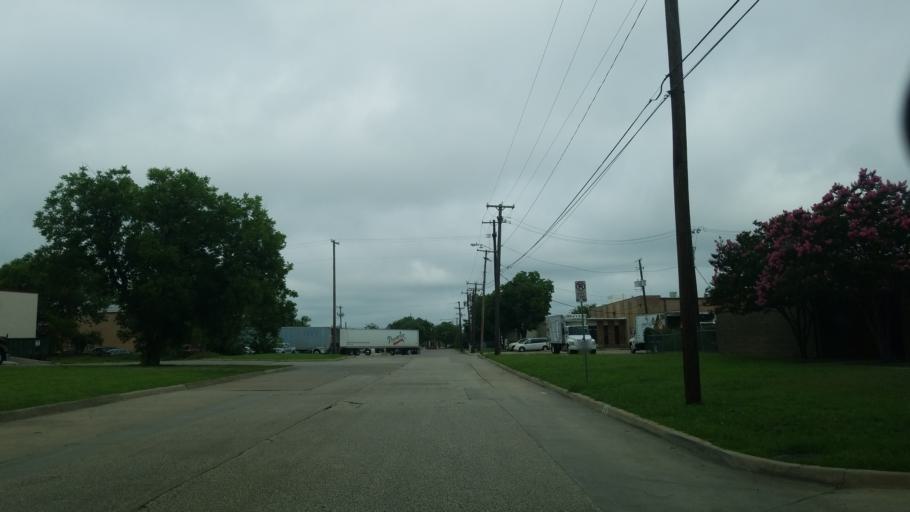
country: US
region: Texas
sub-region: Dallas County
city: Irving
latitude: 32.8373
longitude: -96.8802
